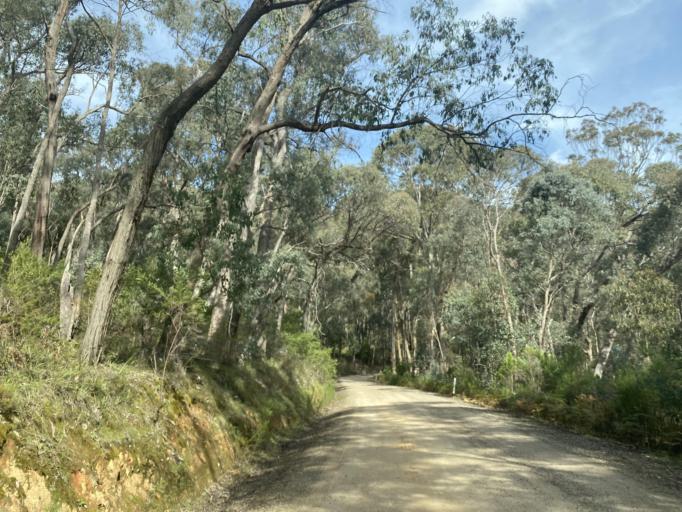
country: AU
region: Victoria
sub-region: Mansfield
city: Mansfield
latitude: -36.8339
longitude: 146.1675
